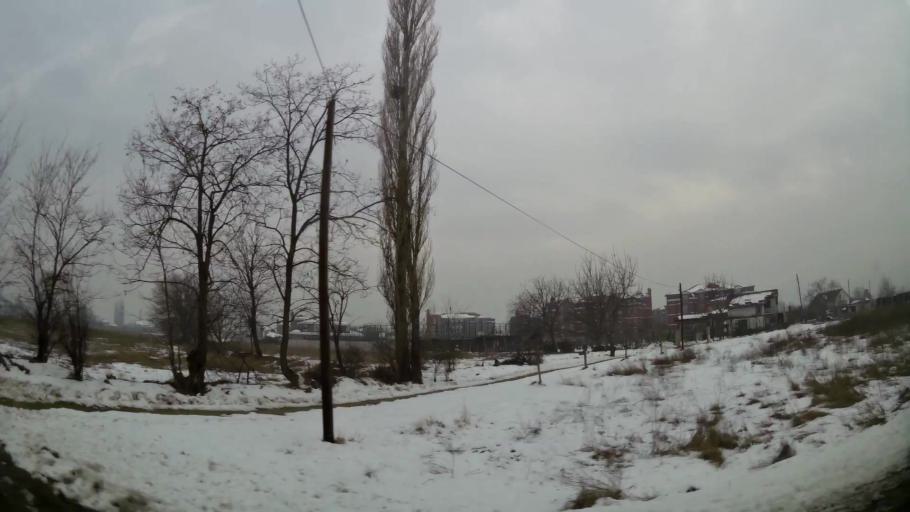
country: MK
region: Cucer-Sandevo
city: Chucher - Sandevo
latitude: 42.0503
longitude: 21.3651
